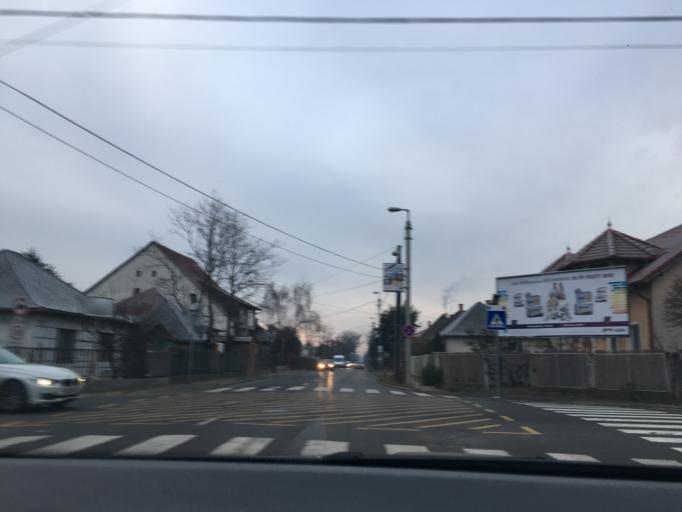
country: HU
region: Hajdu-Bihar
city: Debrecen
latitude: 47.5393
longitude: 21.6597
